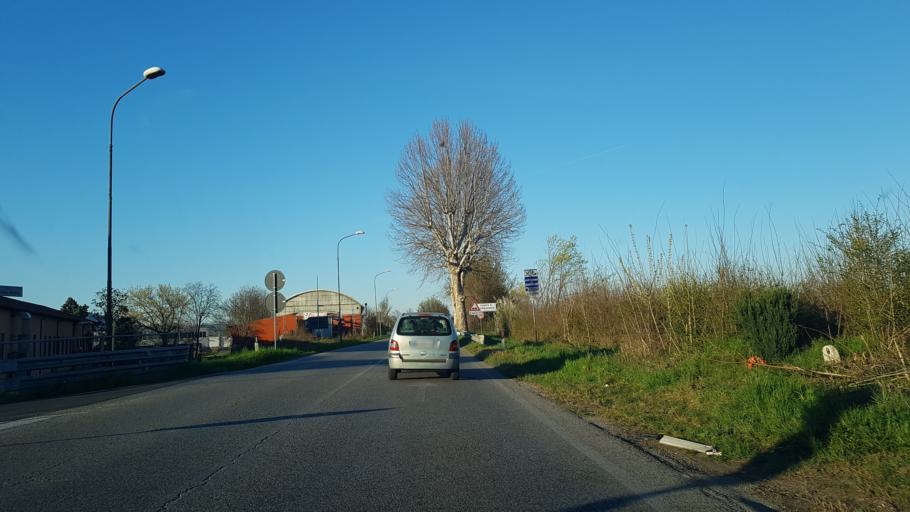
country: IT
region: Veneto
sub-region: Provincia di Vicenza
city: Ponte di Barbarano
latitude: 45.3858
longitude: 11.5721
